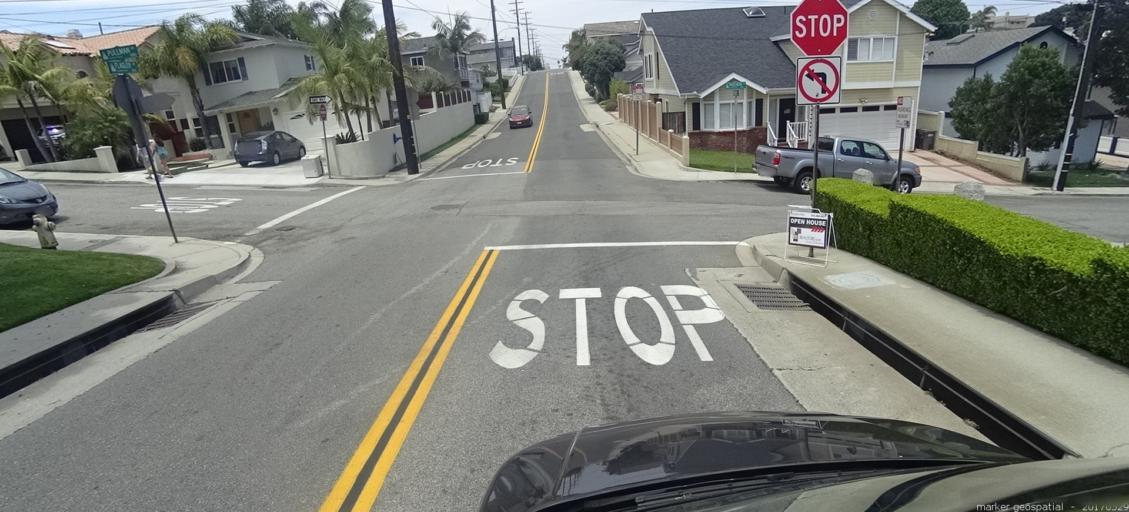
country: US
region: California
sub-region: Los Angeles County
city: Redondo Beach
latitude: 33.8641
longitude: -118.3790
